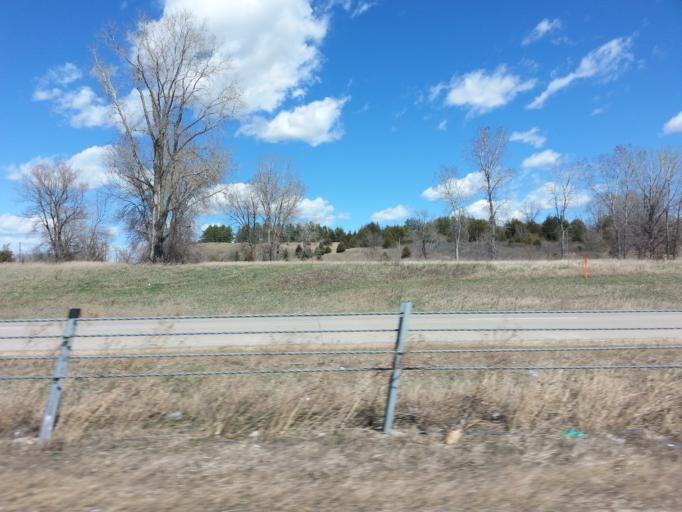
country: US
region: Minnesota
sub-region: Washington County
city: Cottage Grove
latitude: 44.8046
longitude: -92.9116
